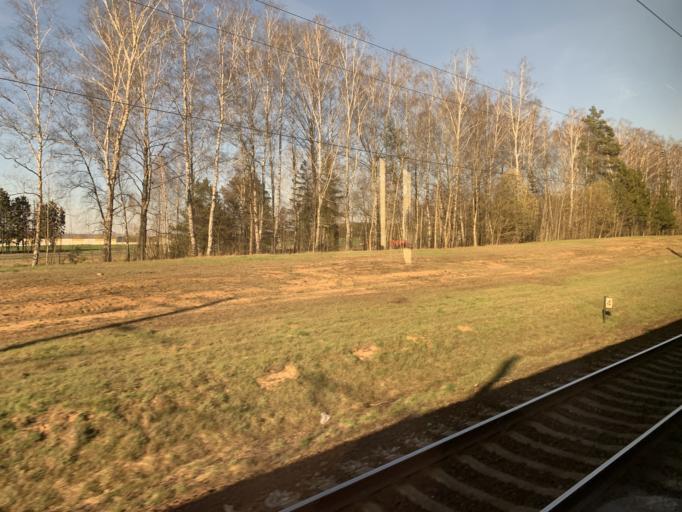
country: BY
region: Minsk
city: Maladzyechna
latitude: 54.2835
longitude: 26.9556
